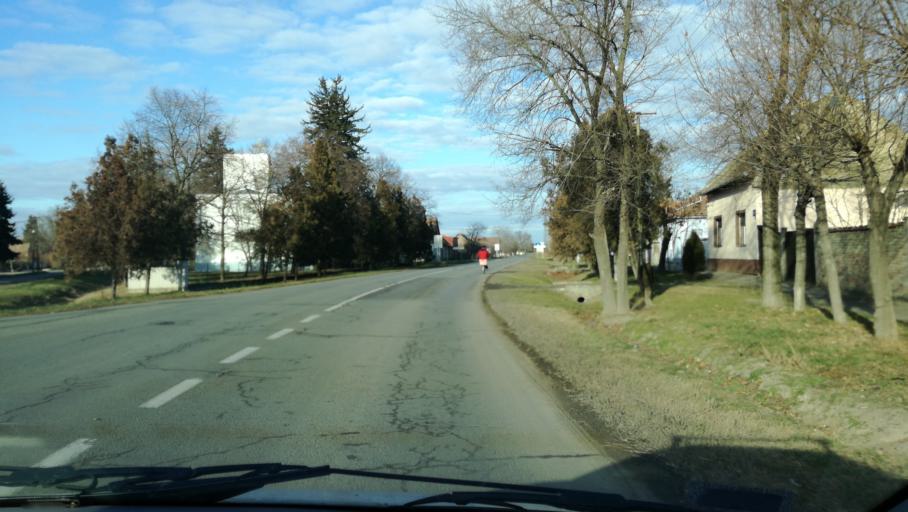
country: RS
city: Ostojicevo
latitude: 45.8906
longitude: 20.1646
